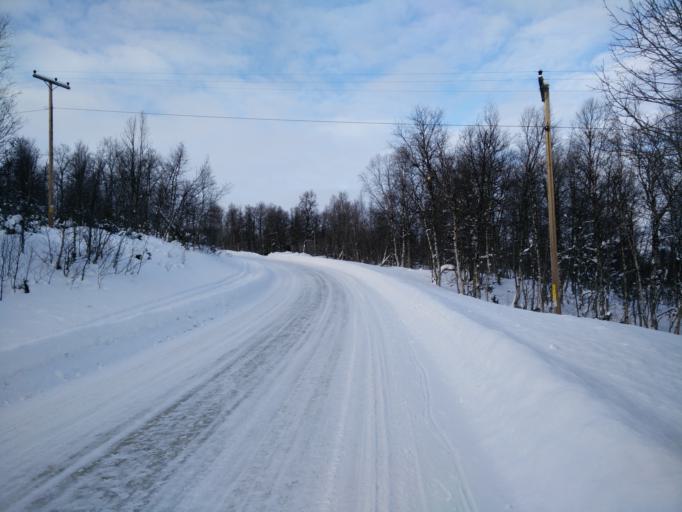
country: NO
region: Sor-Trondelag
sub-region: Tydal
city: Aas
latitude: 62.6503
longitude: 12.4119
